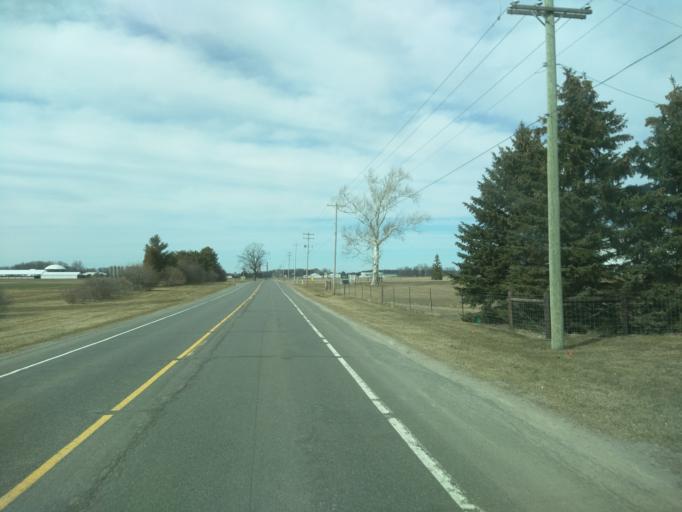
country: US
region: Michigan
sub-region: Ingham County
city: East Lansing
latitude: 42.6903
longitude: -84.4840
